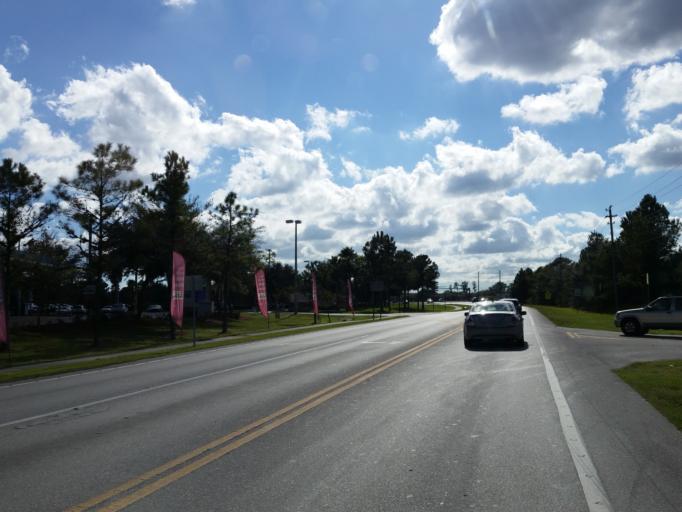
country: US
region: Florida
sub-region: Hillsborough County
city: Fish Hawk
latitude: 27.8626
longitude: -82.2011
